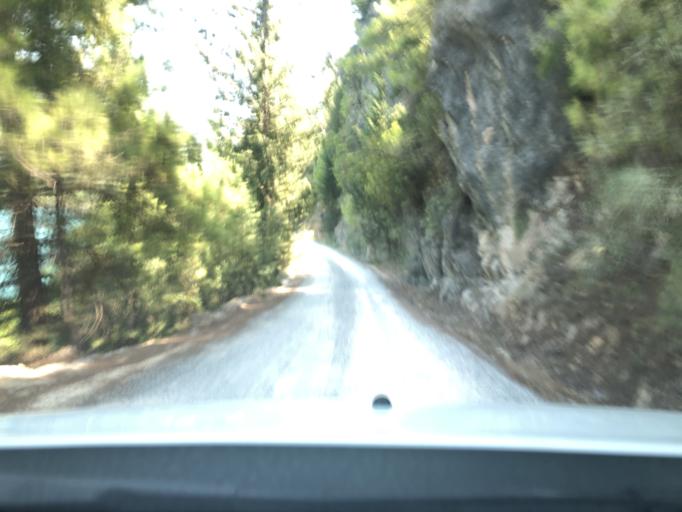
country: TR
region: Antalya
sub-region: Manavgat
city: Manavgat
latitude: 36.9065
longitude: 31.5568
